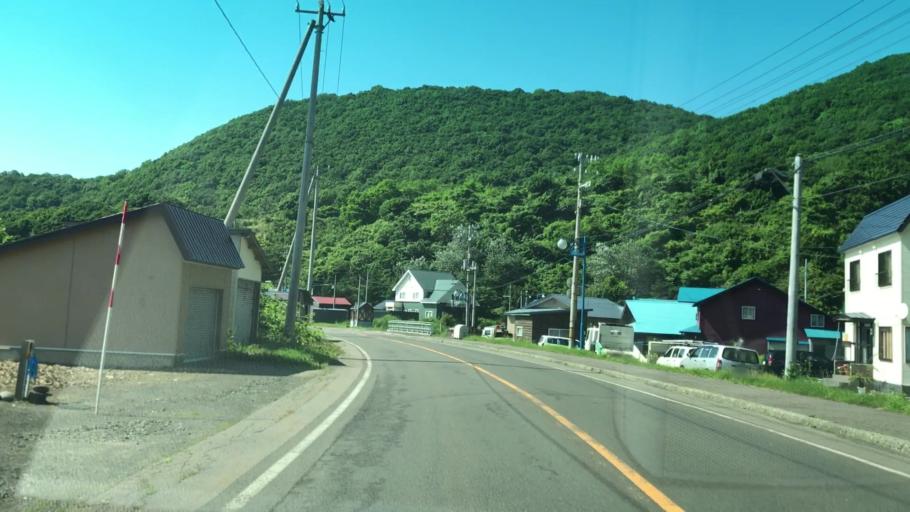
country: JP
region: Hokkaido
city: Iwanai
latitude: 43.1054
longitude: 140.4594
